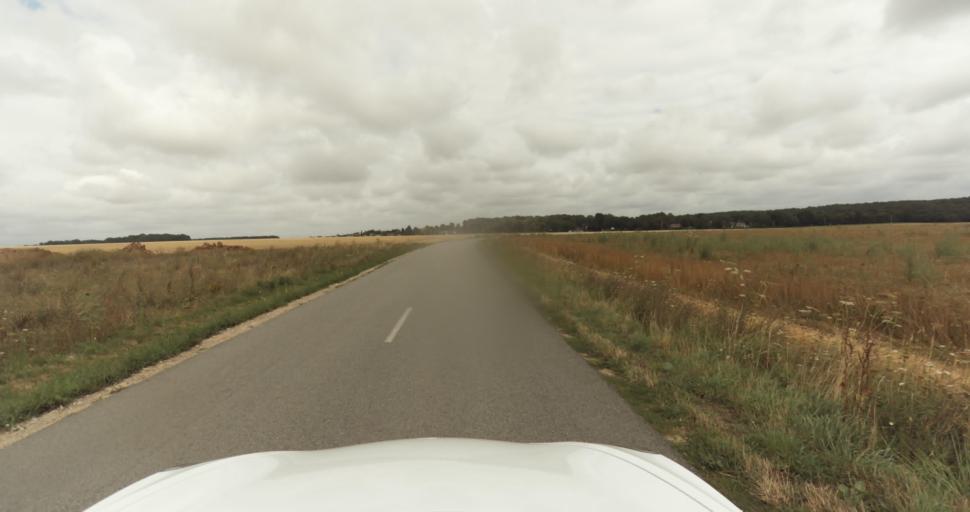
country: FR
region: Haute-Normandie
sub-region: Departement de l'Eure
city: Claville
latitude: 49.0142
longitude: 1.0340
